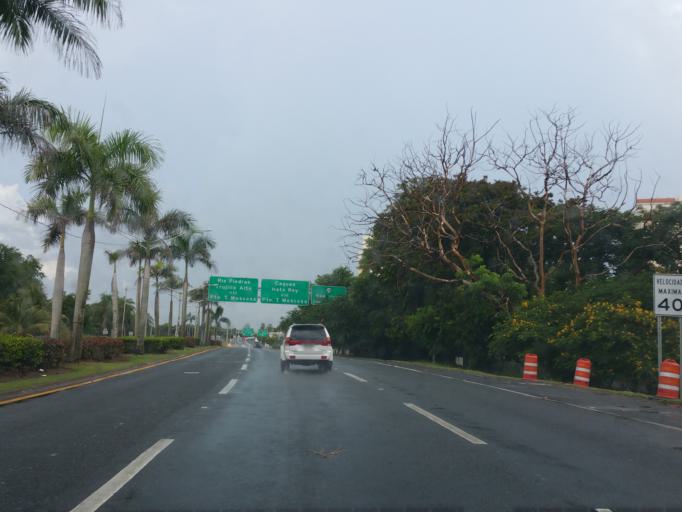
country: PR
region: Carolina
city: Carolina
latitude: 18.4408
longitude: -66.0164
